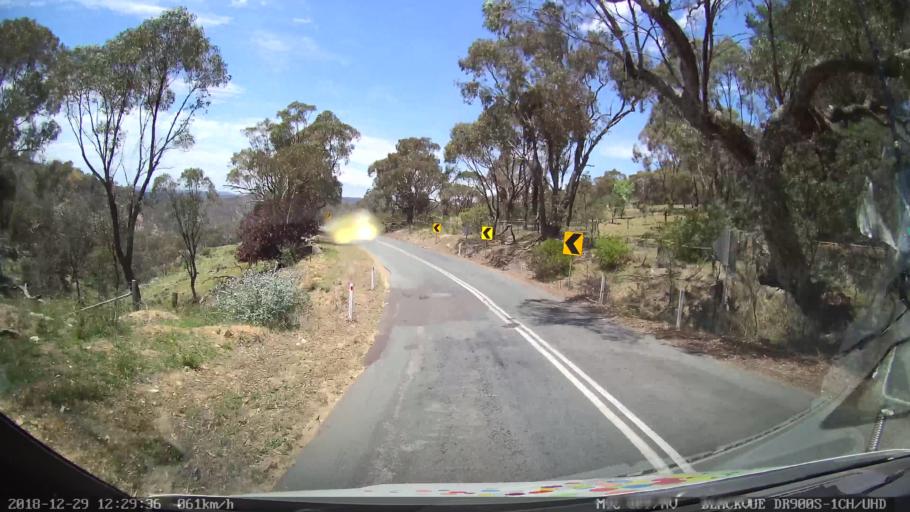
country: AU
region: Australian Capital Territory
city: Macarthur
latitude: -35.4994
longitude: 149.2306
